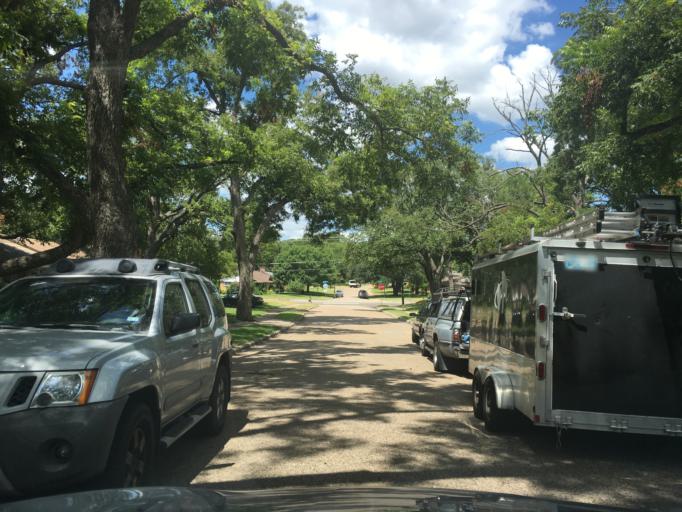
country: US
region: Texas
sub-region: Dallas County
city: Richardson
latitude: 32.8687
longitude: -96.7160
